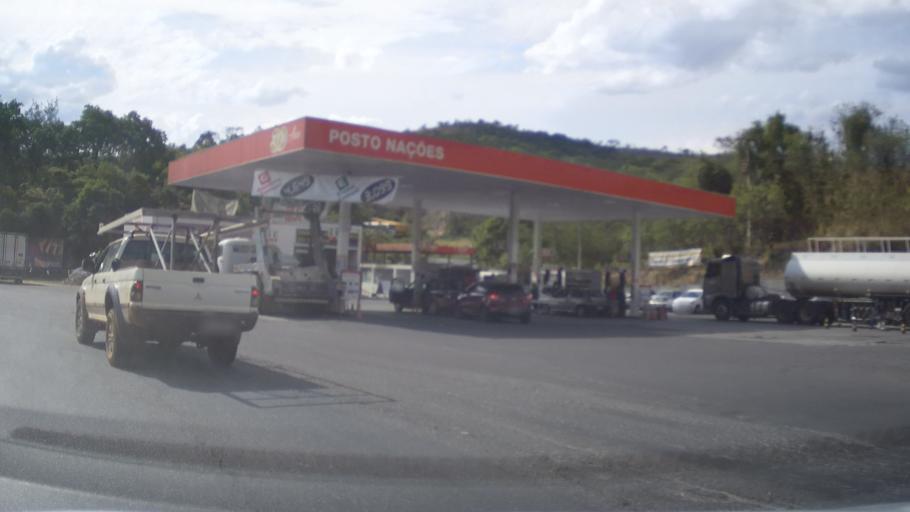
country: BR
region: Minas Gerais
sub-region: Belo Horizonte
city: Belo Horizonte
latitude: -19.8754
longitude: -43.8737
